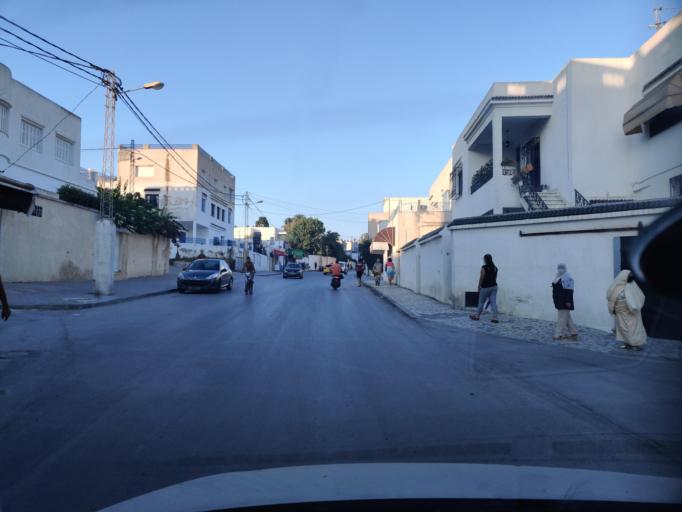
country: TN
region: Tunis
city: Al Marsa
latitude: 36.8883
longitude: 10.3202
